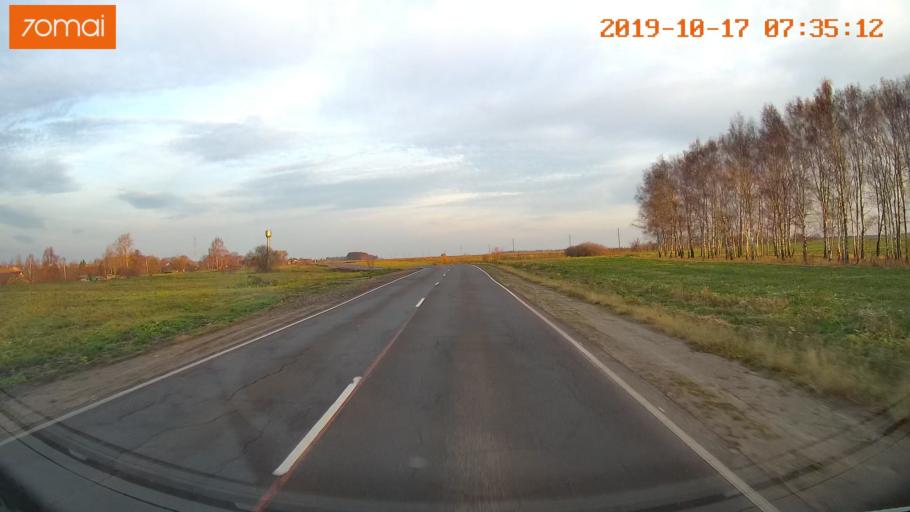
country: RU
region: Ivanovo
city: Gavrilov Posad
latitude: 56.4255
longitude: 39.9320
